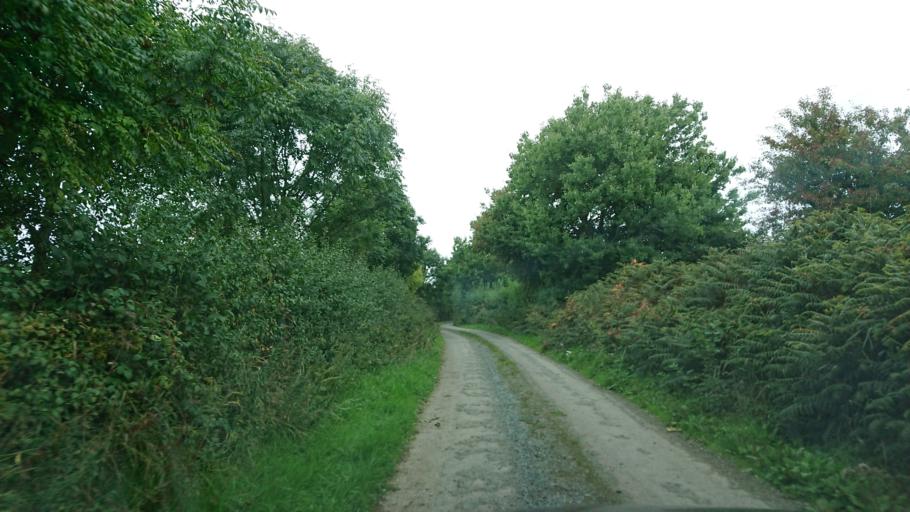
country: IE
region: Munster
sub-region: Waterford
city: Dunmore East
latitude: 52.2001
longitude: -7.0465
